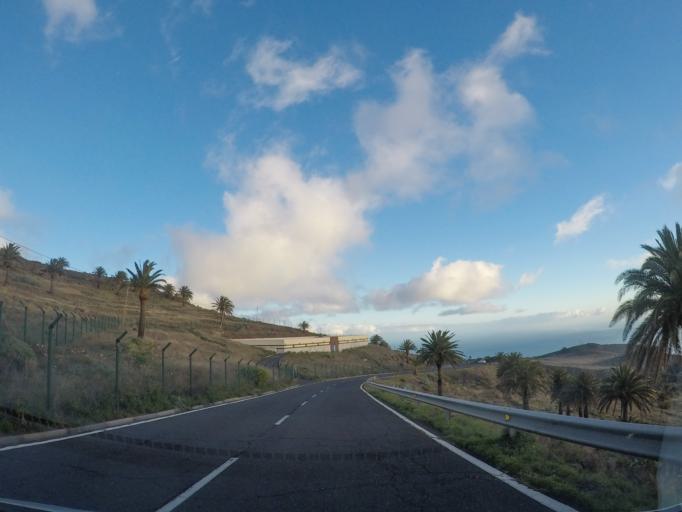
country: ES
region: Canary Islands
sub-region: Provincia de Santa Cruz de Tenerife
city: Alajero
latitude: 28.0774
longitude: -17.2428
